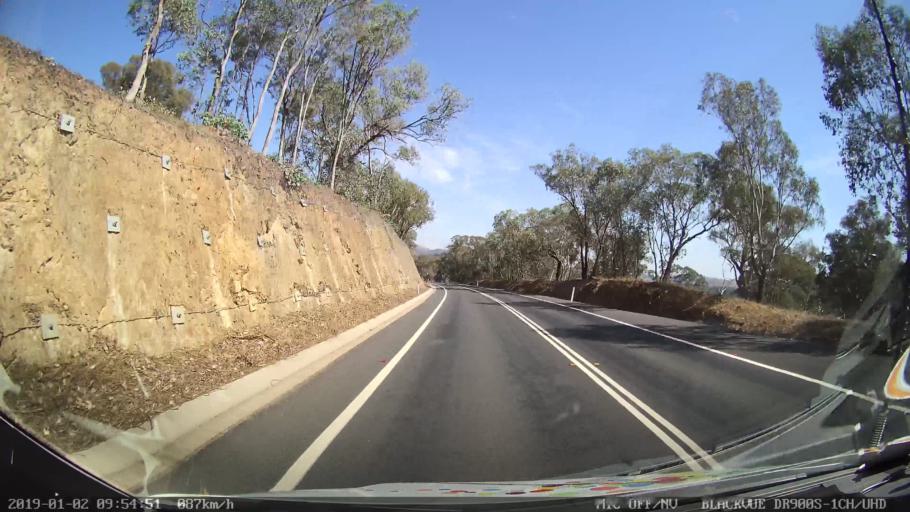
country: AU
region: New South Wales
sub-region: Tumut Shire
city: Tumut
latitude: -35.2298
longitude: 148.1946
